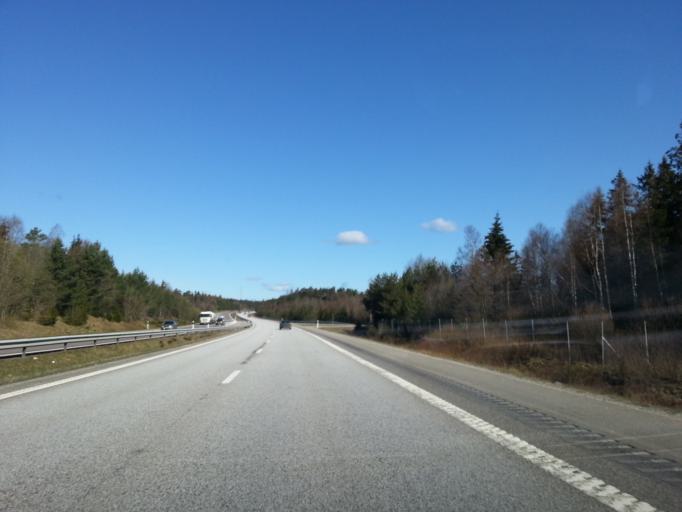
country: SE
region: Vaestra Goetaland
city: Svanesund
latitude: 58.1005
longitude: 11.8825
